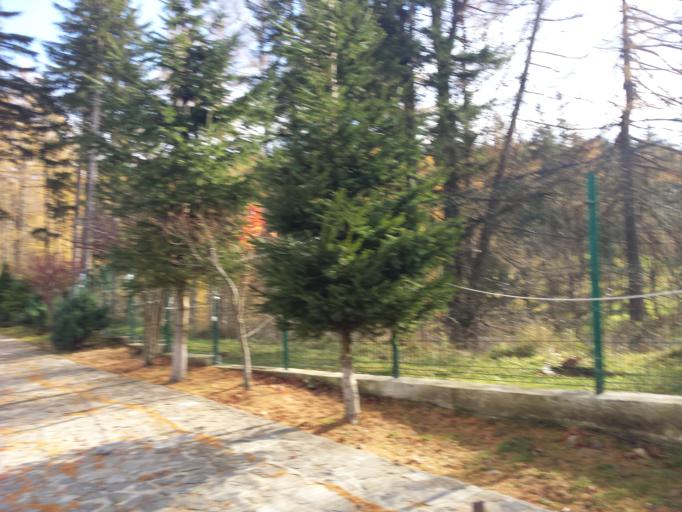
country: RO
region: Prahova
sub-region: Oras Busteni
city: Busteni
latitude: 45.4051
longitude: 25.5404
